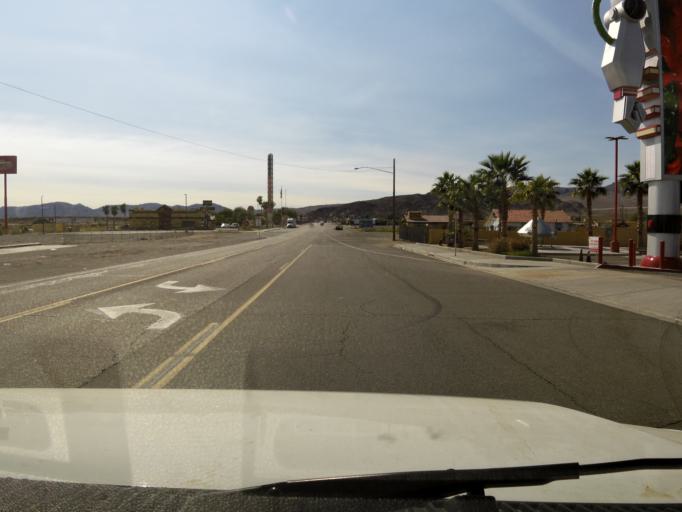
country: US
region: California
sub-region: San Bernardino County
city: Fort Irwin
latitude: 35.2682
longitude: -116.0708
